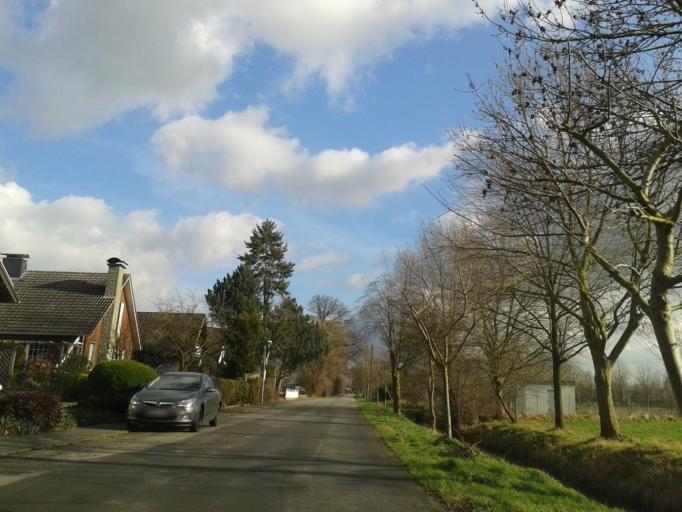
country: DE
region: North Rhine-Westphalia
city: Geseke
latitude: 51.6857
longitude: 8.5049
